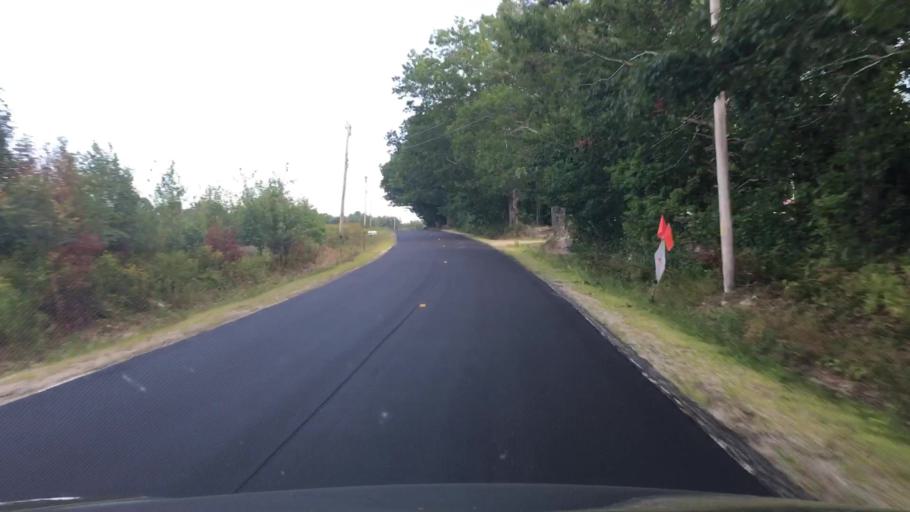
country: US
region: Maine
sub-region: Hancock County
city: Penobscot
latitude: 44.5381
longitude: -68.6154
